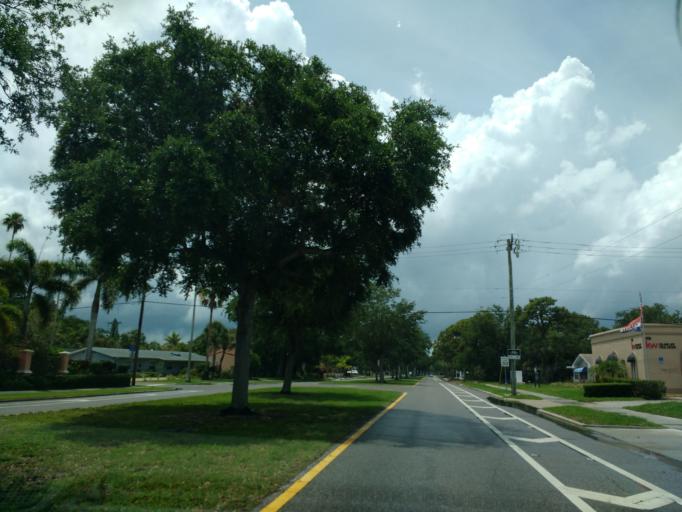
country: US
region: Florida
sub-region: Sarasota County
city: Venice
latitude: 27.0984
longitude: -82.4501
